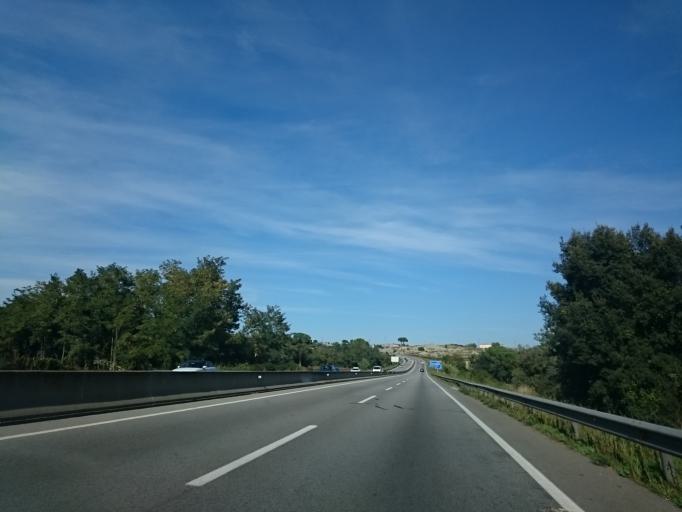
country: ES
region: Catalonia
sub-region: Provincia de Barcelona
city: Centelles
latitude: 41.8145
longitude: 2.2291
